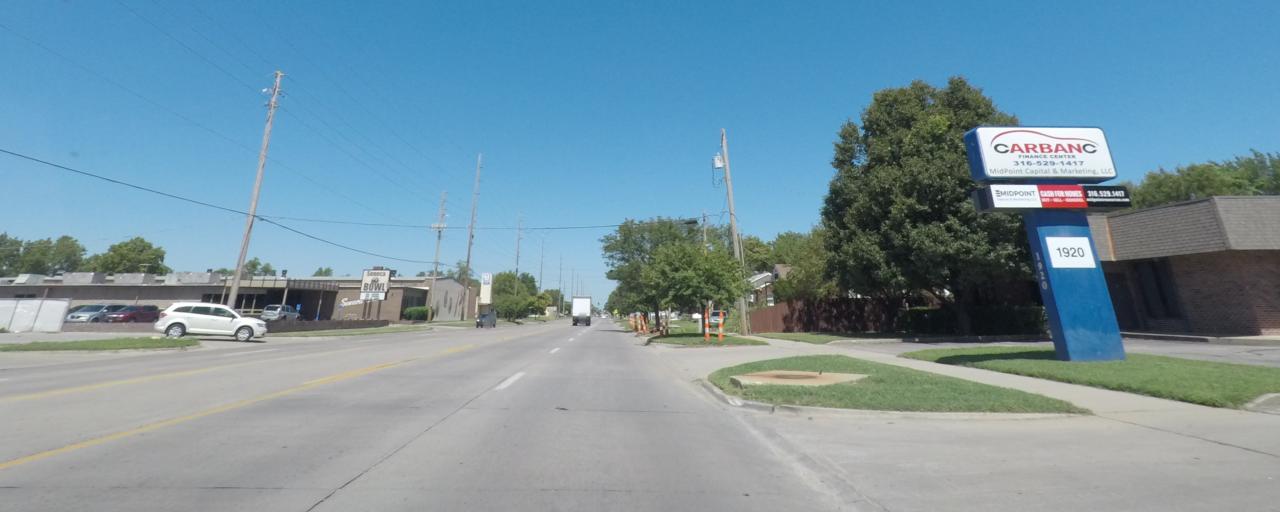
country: US
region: Kansas
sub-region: Sedgwick County
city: Wichita
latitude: 37.6592
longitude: -97.3528
